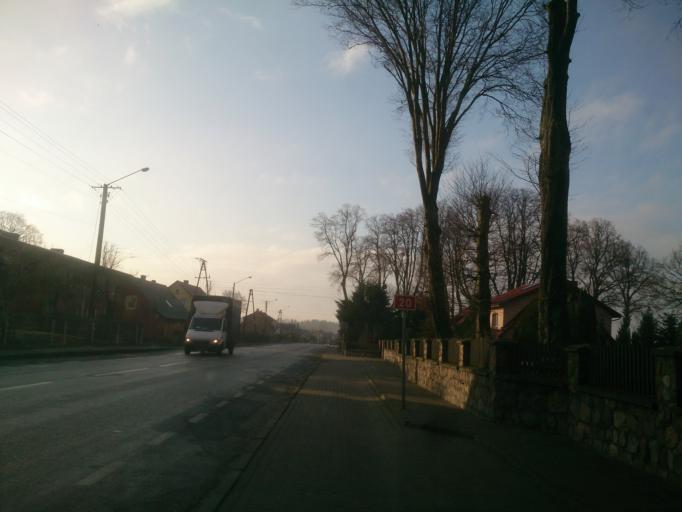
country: PL
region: Pomeranian Voivodeship
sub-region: Powiat bytowski
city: Tuchomie
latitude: 54.0592
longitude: 17.2417
